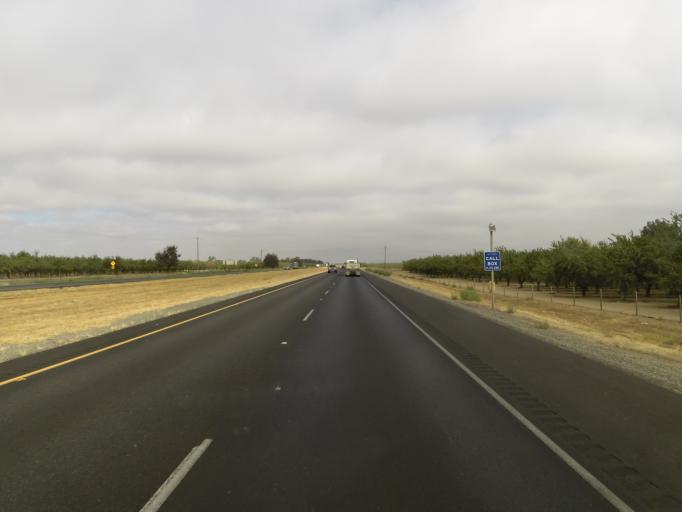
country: US
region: California
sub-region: Yolo County
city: Dunnigan
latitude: 38.9137
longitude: -121.9922
